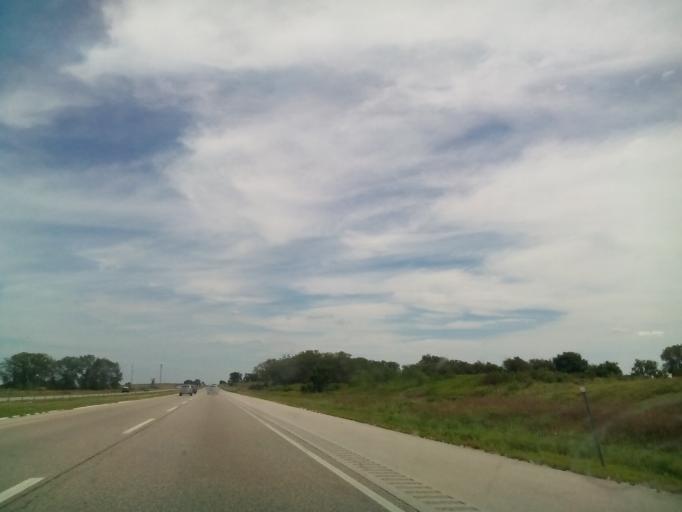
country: US
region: Illinois
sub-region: DeKalb County
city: Cortland
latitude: 41.9007
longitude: -88.6758
